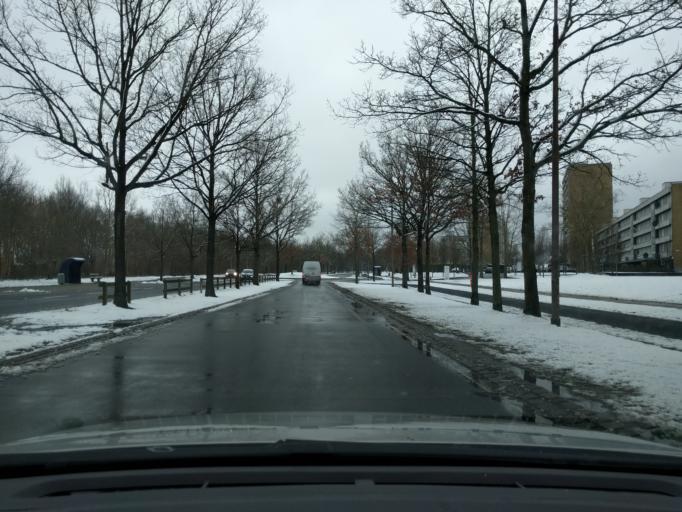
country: DK
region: South Denmark
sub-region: Odense Kommune
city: Seden
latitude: 55.4136
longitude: 10.4400
